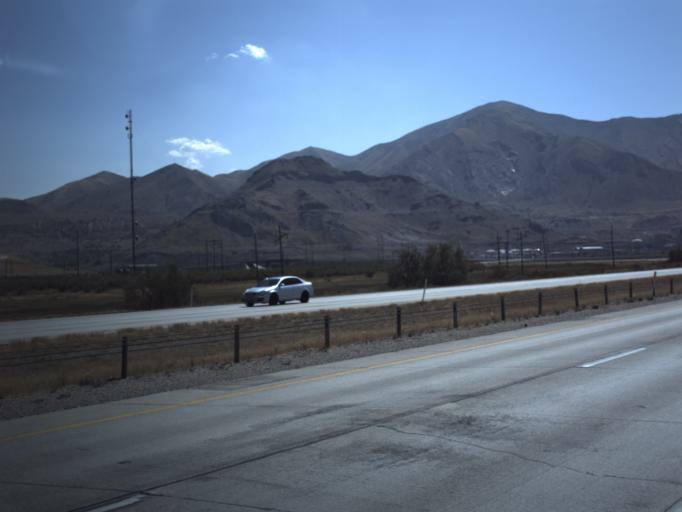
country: US
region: Utah
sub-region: Salt Lake County
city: Magna
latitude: 40.7503
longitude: -112.1773
